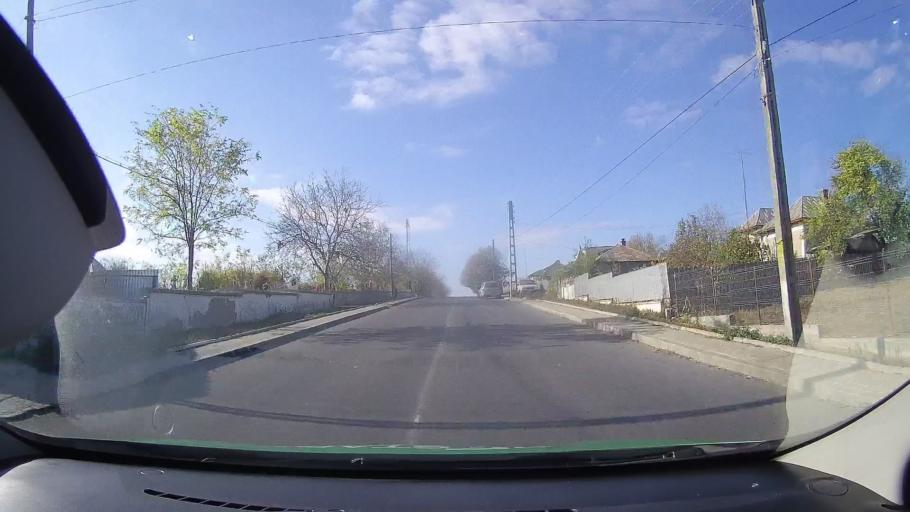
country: RO
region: Tulcea
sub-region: Comuna Valea Nucarilor
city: Valea Nucarilor
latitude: 45.0426
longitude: 28.9341
